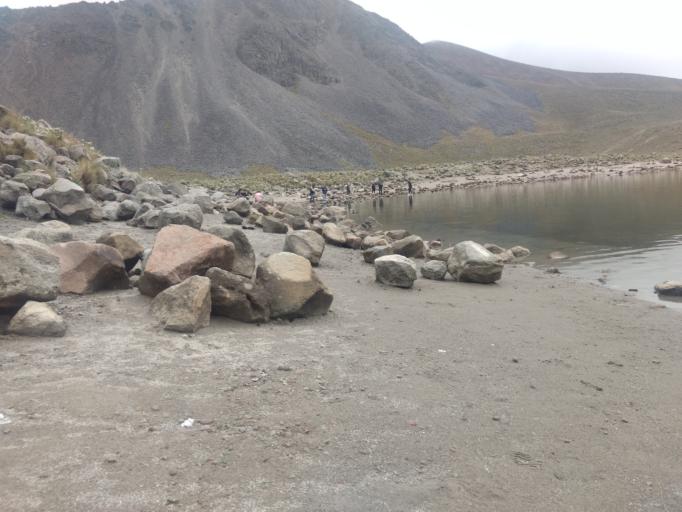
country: MX
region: Mexico
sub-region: Tenango del Valle
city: Santa Cruz Pueblo Nuevo (Pueblo Nuevo)
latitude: 19.1077
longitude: -99.7530
